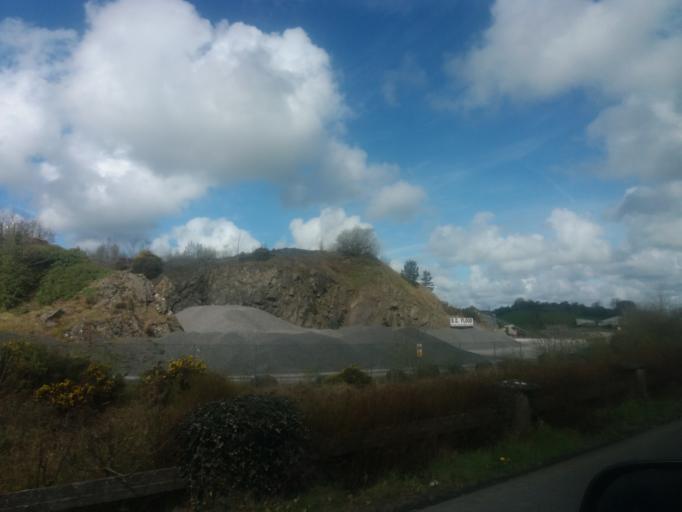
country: IE
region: Ulster
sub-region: An Cabhan
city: Ballyjamesduff
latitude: 53.9326
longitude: -7.2170
